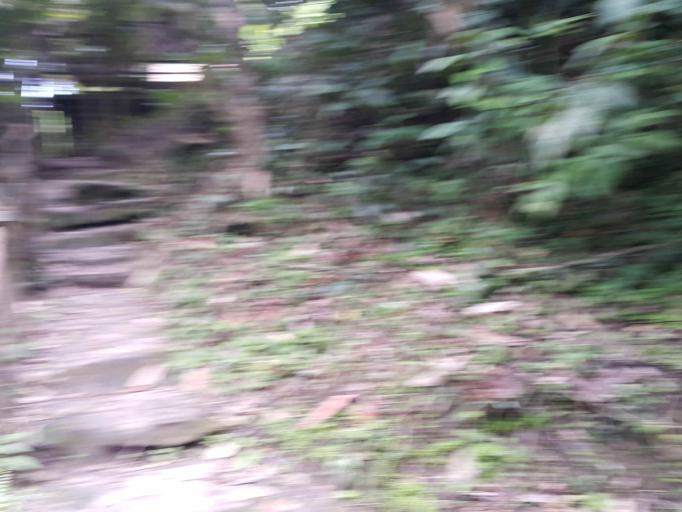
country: TH
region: Chiang Mai
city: Chom Thong
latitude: 18.5421
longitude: 98.5993
